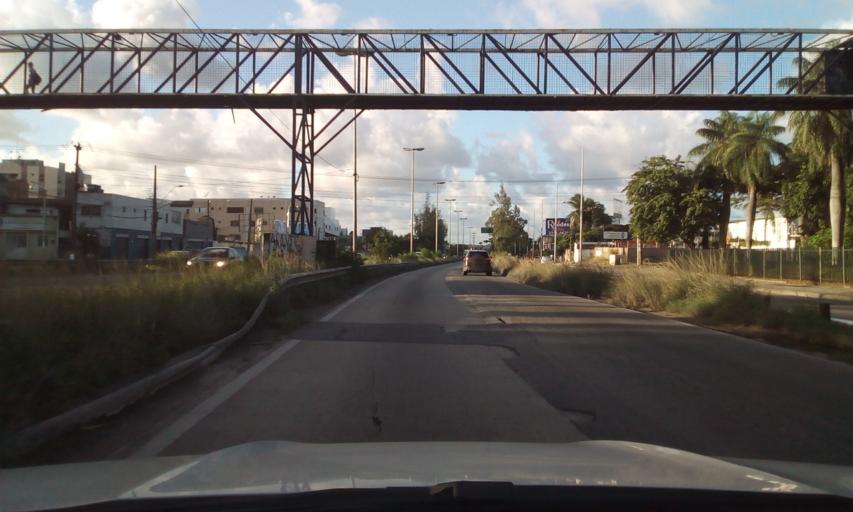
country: BR
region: Pernambuco
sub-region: Recife
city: Recife
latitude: -8.0470
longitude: -34.9451
